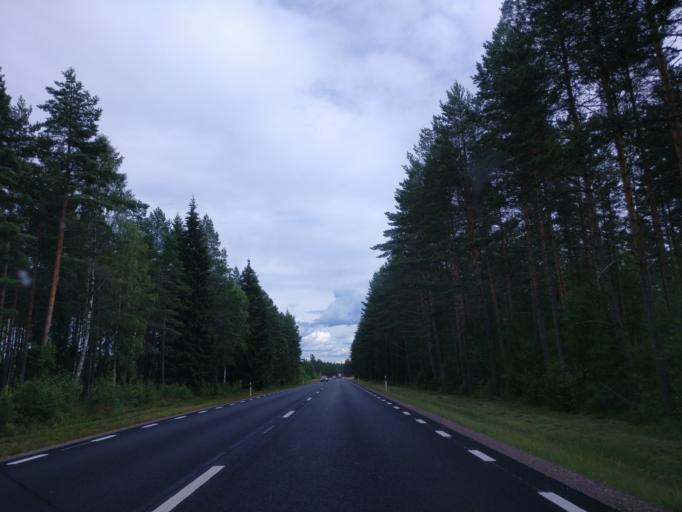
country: SE
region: Vaermland
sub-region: Hagfors Kommun
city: Hagfors
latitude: 60.0506
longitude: 13.5658
